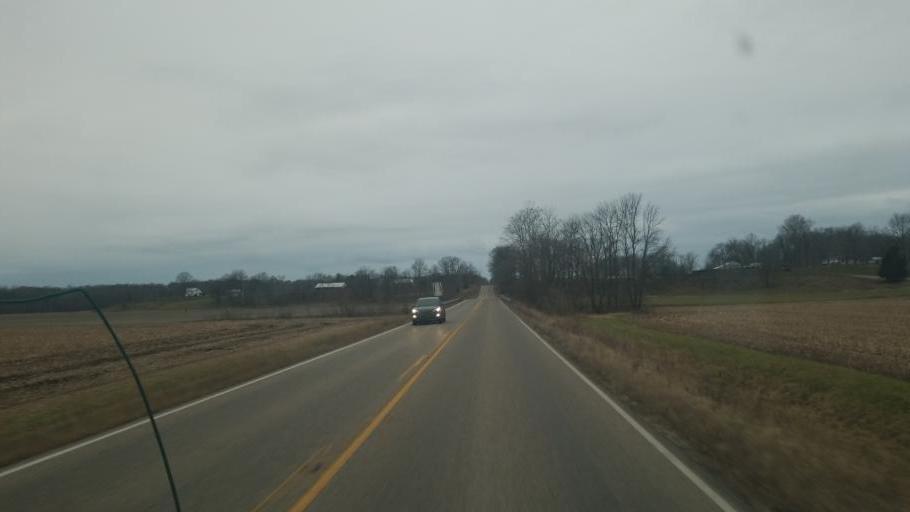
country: US
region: Indiana
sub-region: Clay County
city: Middlebury
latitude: 39.3861
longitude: -87.0334
